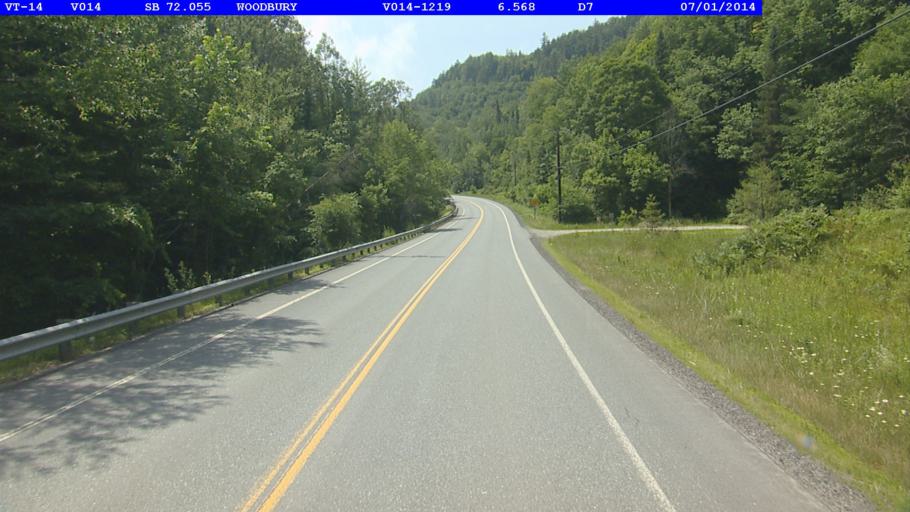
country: US
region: Vermont
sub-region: Caledonia County
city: Hardwick
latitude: 44.4744
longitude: -72.3969
